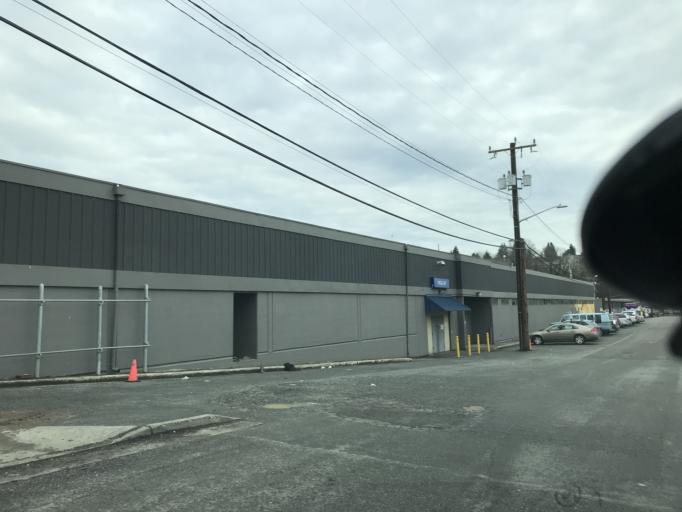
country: US
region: Washington
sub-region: King County
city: Seattle
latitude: 47.5967
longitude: -122.3157
